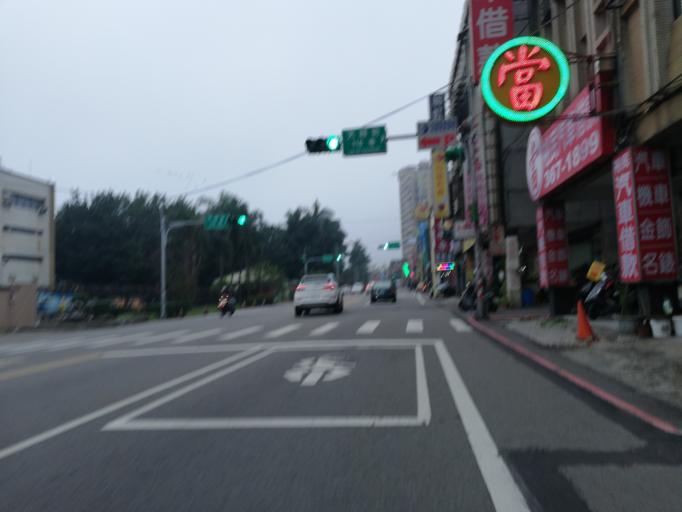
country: TW
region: Taiwan
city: Taoyuan City
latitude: 24.9731
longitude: 121.3022
